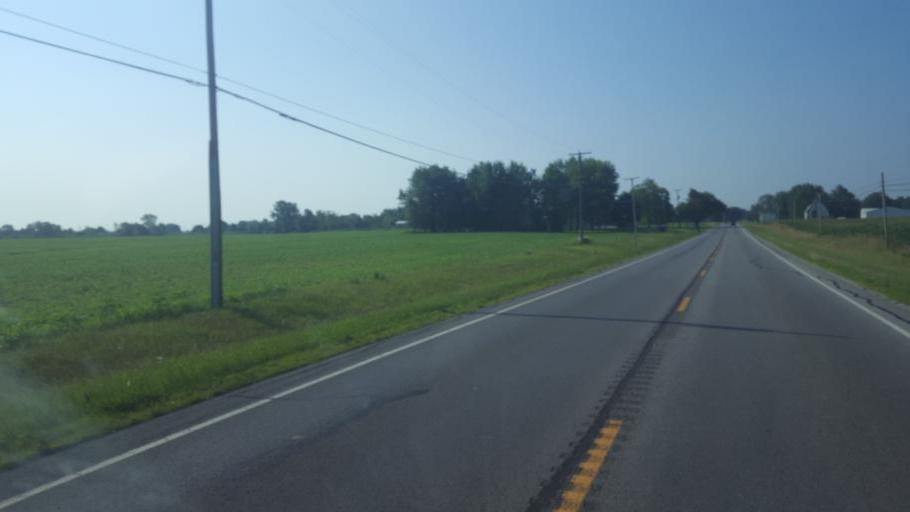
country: US
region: Ohio
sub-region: Hardin County
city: Kenton
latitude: 40.6670
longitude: -83.6105
